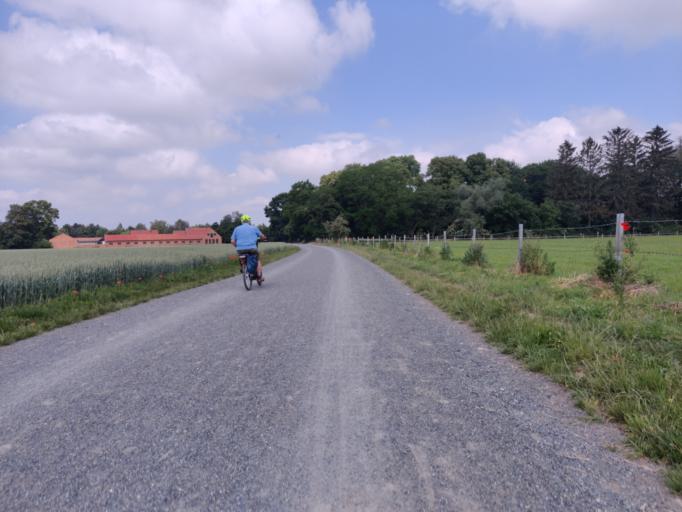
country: DE
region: Lower Saxony
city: Hildesheim
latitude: 52.1126
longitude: 9.9834
